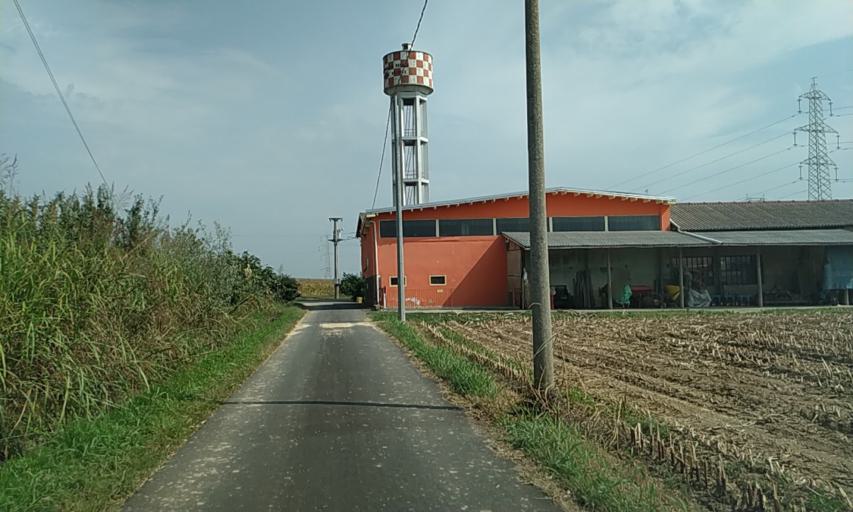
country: IT
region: Piedmont
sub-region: Provincia di Vercelli
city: Livorno Ferraris
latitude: 45.3163
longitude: 8.0716
